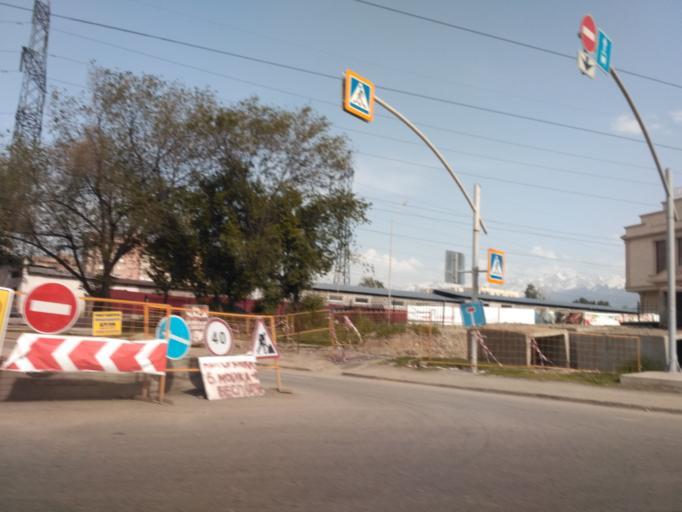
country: KZ
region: Almaty Qalasy
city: Almaty
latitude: 43.2437
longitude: 76.8493
